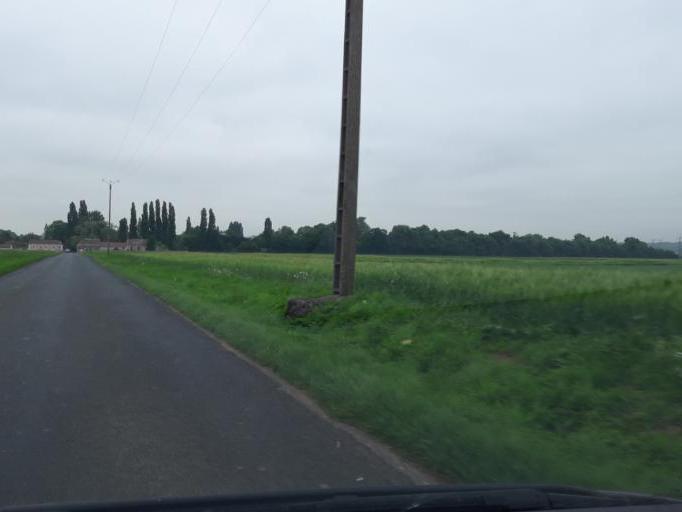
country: FR
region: Ile-de-France
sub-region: Departement de l'Essonne
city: Vert-le-Grand
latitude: 48.5627
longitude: 2.3533
